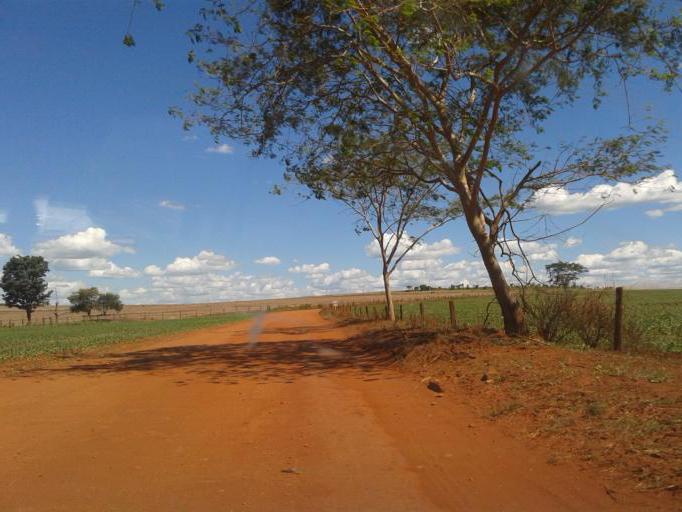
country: BR
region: Minas Gerais
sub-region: Capinopolis
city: Capinopolis
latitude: -18.6557
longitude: -49.5822
